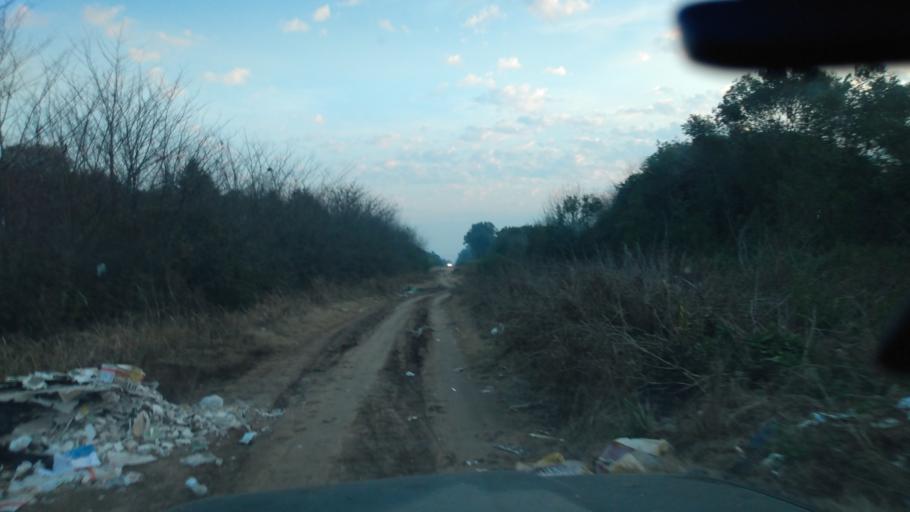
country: AR
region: Buenos Aires
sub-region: Partido de Lujan
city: Lujan
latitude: -34.5509
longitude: -59.1423
